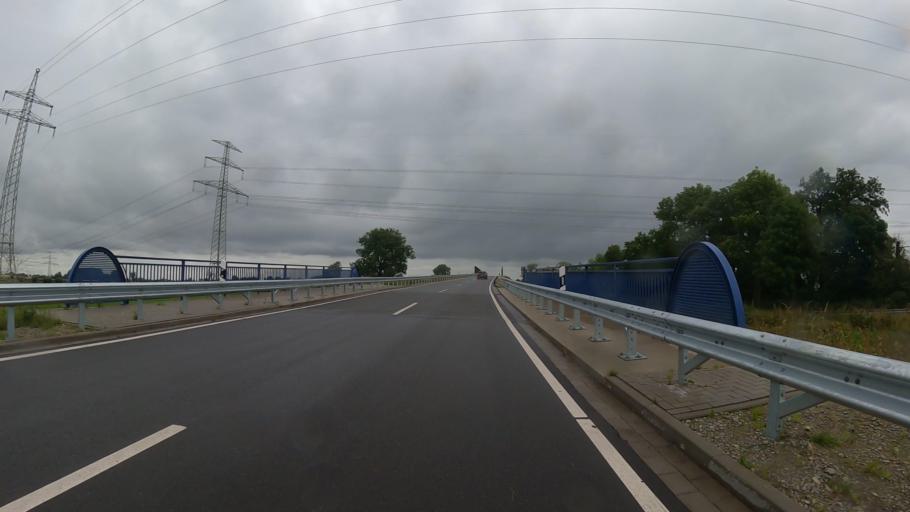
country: DE
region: Lower Saxony
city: Neu Wulmstorf
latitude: 53.4849
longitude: 9.7462
